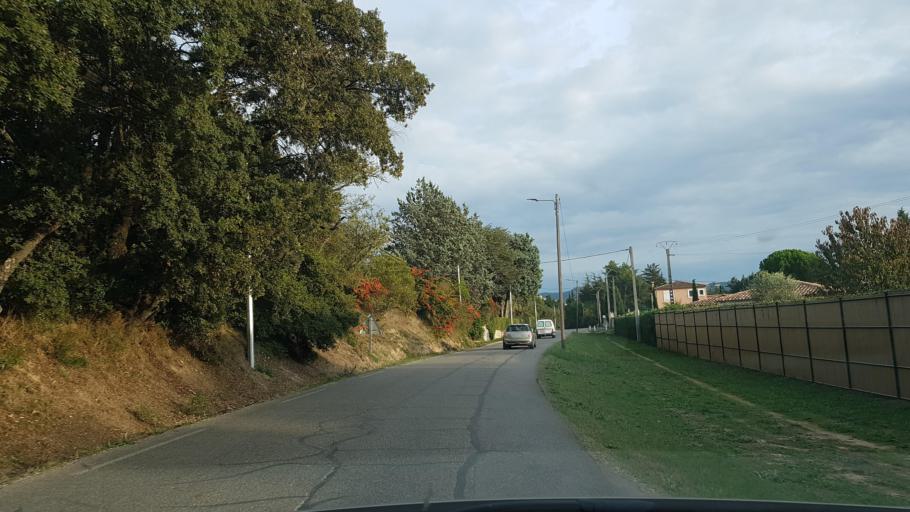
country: FR
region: Provence-Alpes-Cote d'Azur
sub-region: Departement des Bouches-du-Rhone
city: Cabries
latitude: 43.4473
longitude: 5.3681
